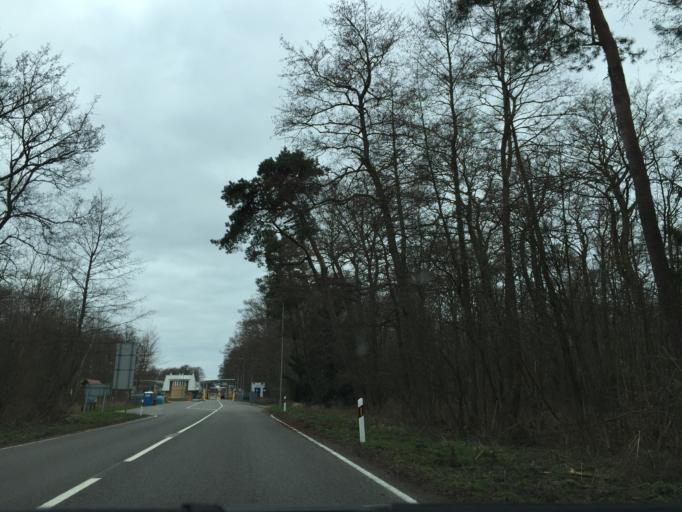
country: LT
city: Nida
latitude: 55.2826
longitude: 20.9673
